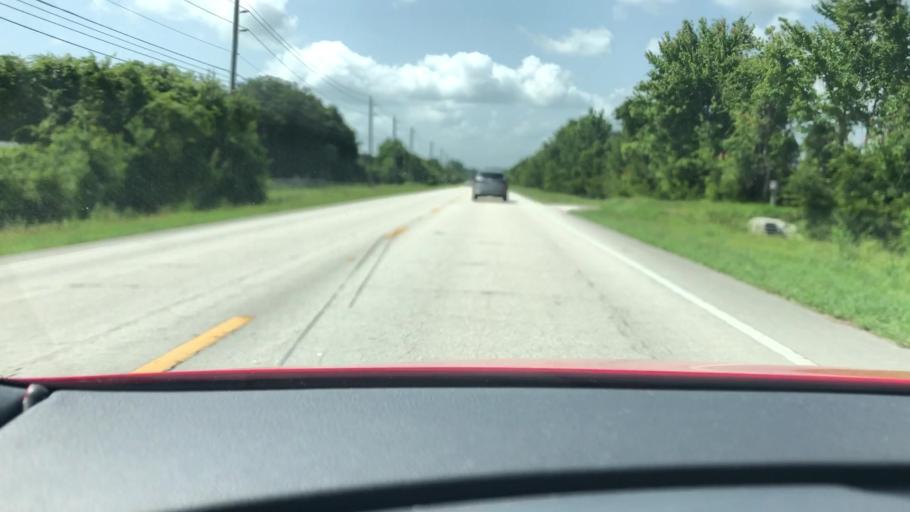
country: US
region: Florida
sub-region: Volusia County
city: Samsula-Spruce Creek
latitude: 29.0699
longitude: -81.0681
